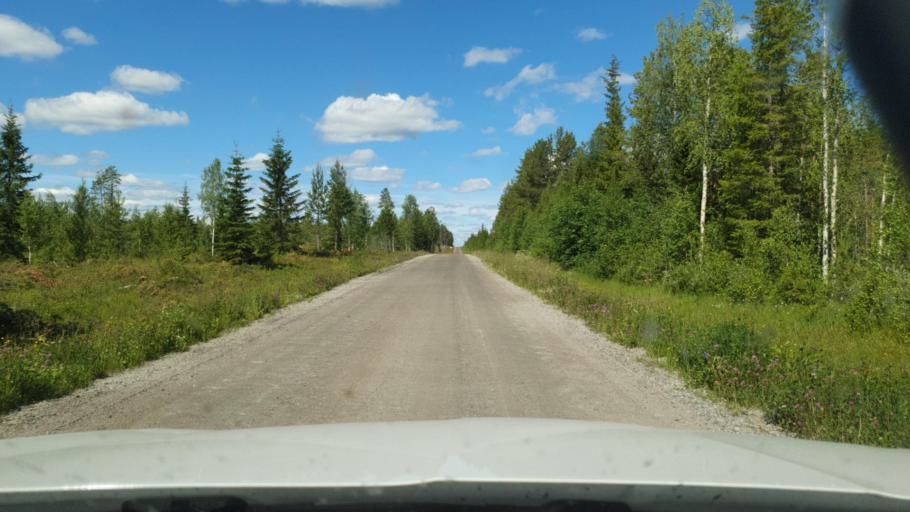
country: SE
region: Vaesterbotten
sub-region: Skelleftea Kommun
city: Byske
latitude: 65.1282
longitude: 21.2023
